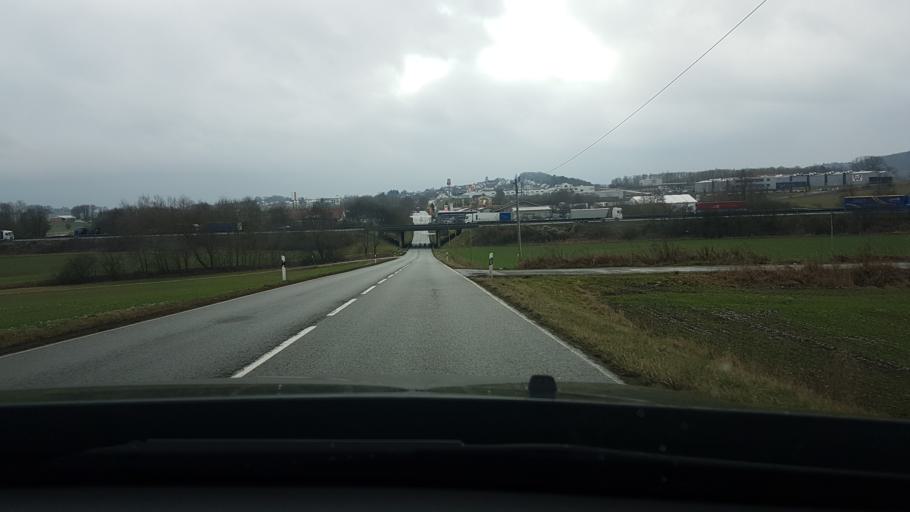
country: DE
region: Hesse
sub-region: Regierungsbezirk Kassel
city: Bad Arolsen
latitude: 51.4934
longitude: 9.0066
